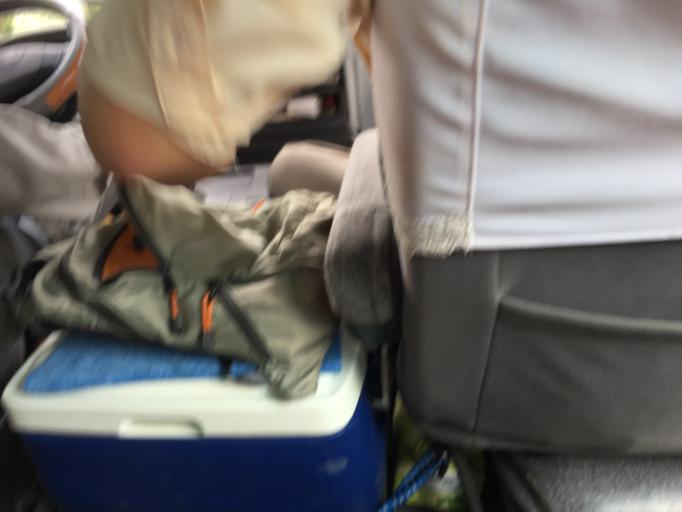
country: KH
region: Phnom Penh
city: Phnom Penh
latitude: 11.5559
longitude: 104.9208
